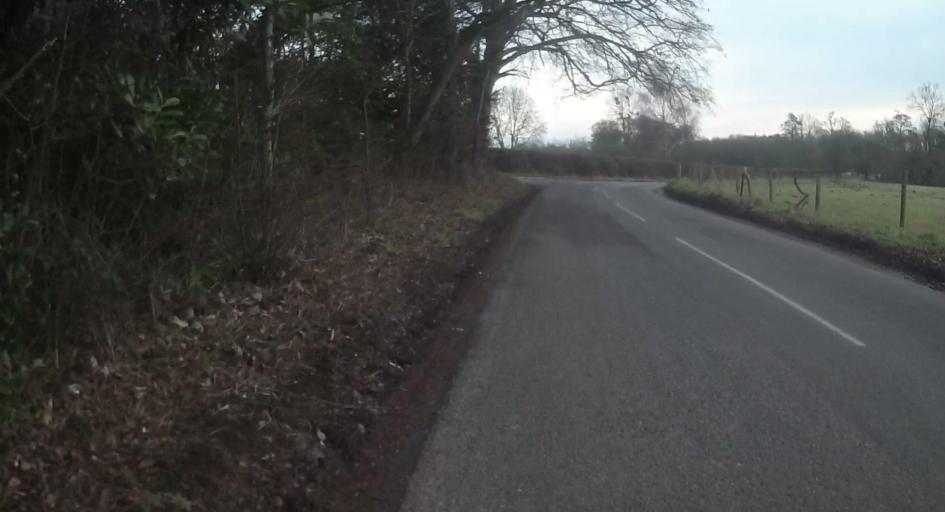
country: GB
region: England
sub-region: Hampshire
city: Highclere
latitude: 51.2250
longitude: -1.3784
